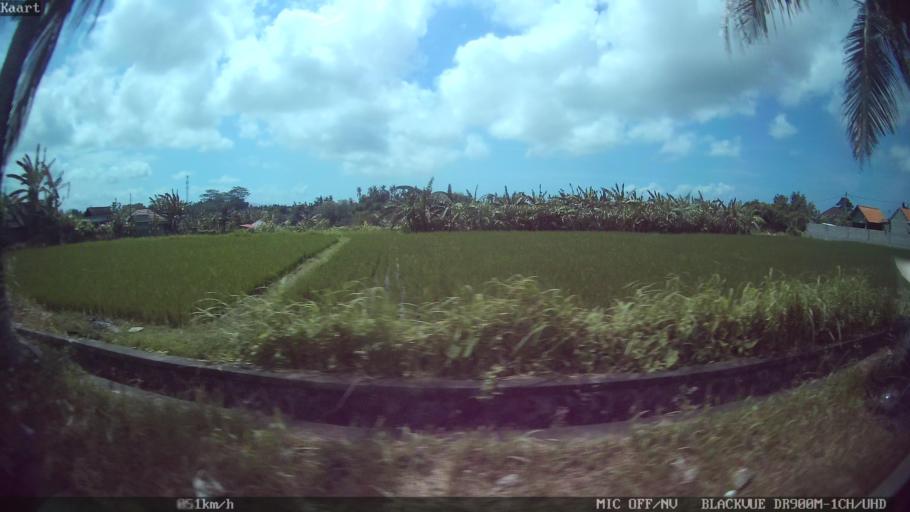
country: ID
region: Bali
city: Banjar Desa
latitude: -8.5810
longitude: 115.2877
